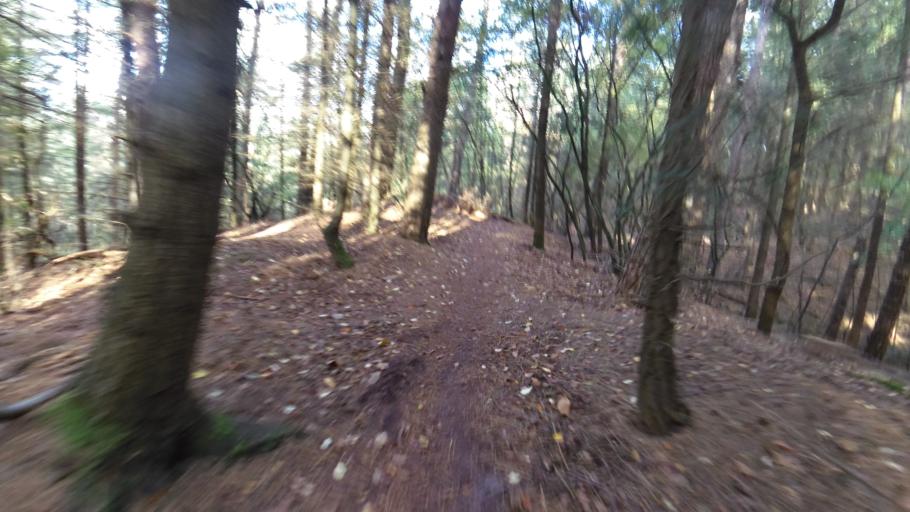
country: NL
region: Gelderland
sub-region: Gemeente Nunspeet
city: Nunspeet
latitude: 52.3656
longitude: 5.8158
